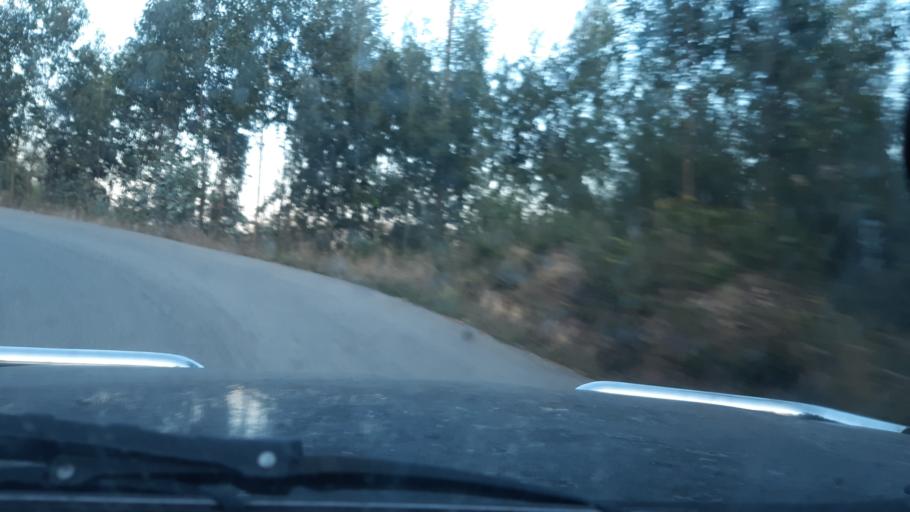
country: PT
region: Aveiro
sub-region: Agueda
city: Aguada de Cima
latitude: 40.5677
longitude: -8.3642
